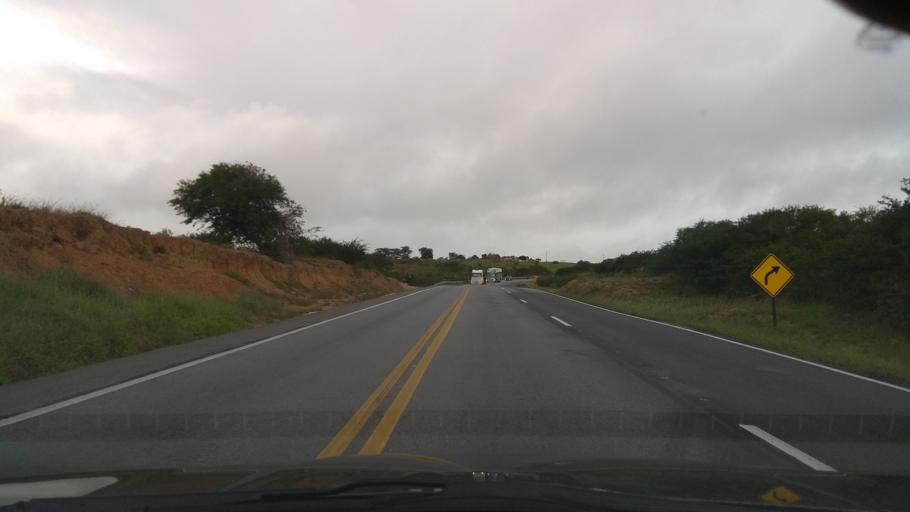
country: BR
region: Bahia
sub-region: Santa Ines
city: Santa Ines
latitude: -13.0577
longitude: -39.9576
